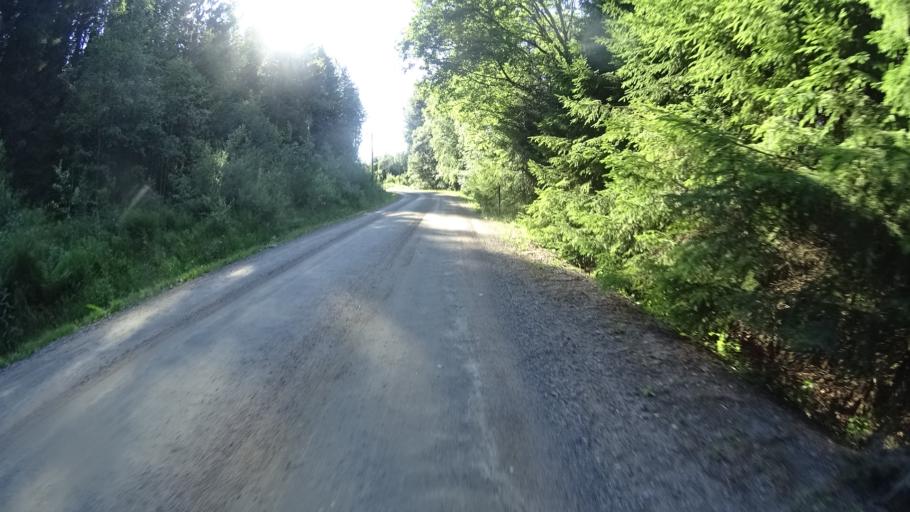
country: FI
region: Uusimaa
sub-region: Helsinki
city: Karkkila
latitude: 60.6479
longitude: 24.1517
